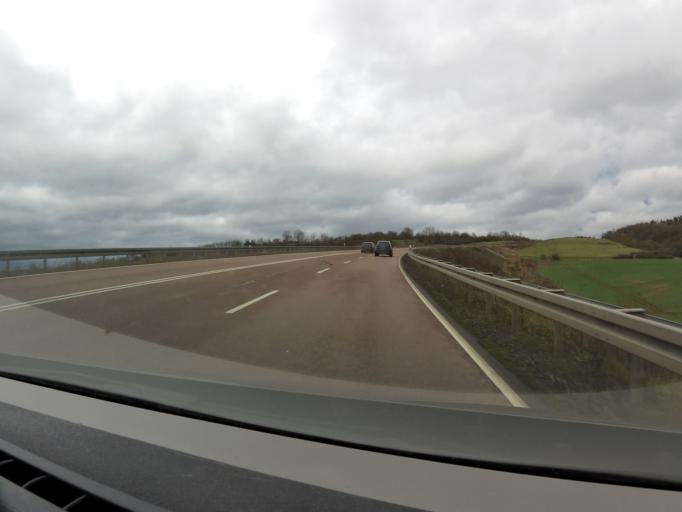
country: DE
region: Saxony-Anhalt
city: Riestedt
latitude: 51.5049
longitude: 11.3756
